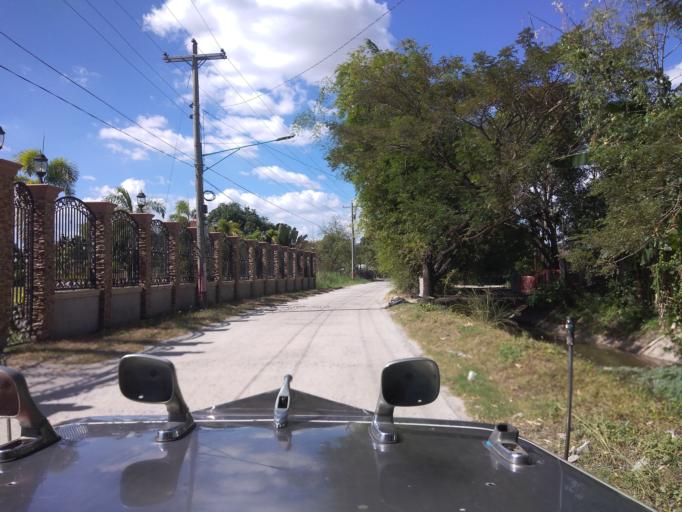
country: PH
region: Central Luzon
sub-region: Province of Pampanga
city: Bacolor
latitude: 15.0101
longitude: 120.6445
